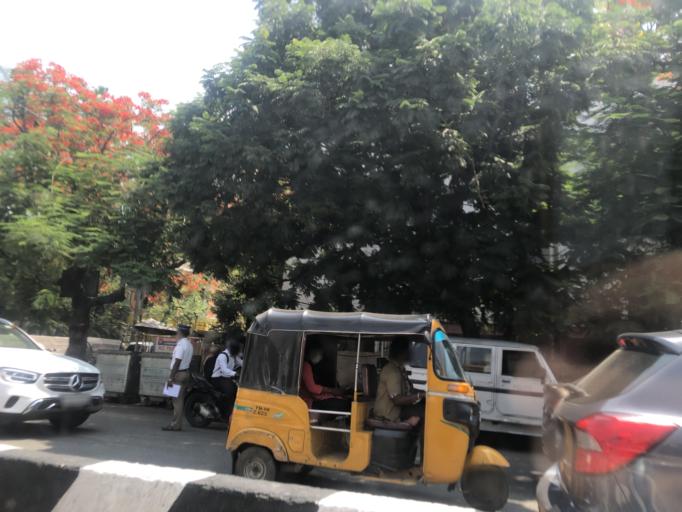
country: IN
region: Tamil Nadu
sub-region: Chennai
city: Gandhi Nagar
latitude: 12.9837
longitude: 80.2595
